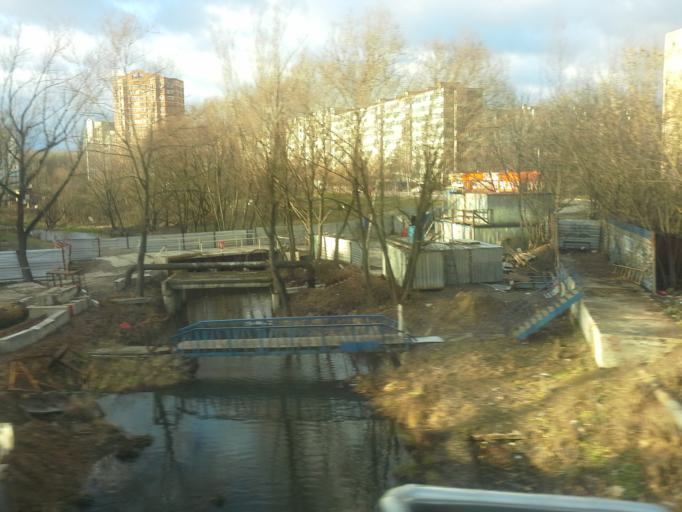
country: RU
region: Moskovskaya
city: Mytishchi
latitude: 55.9097
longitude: 37.7550
